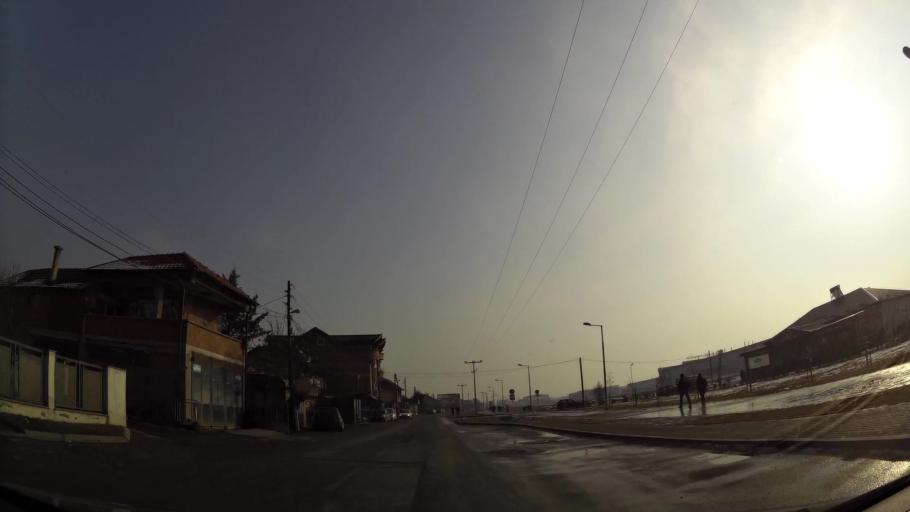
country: MK
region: Ilinden
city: Marino
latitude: 41.9867
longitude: 21.5889
